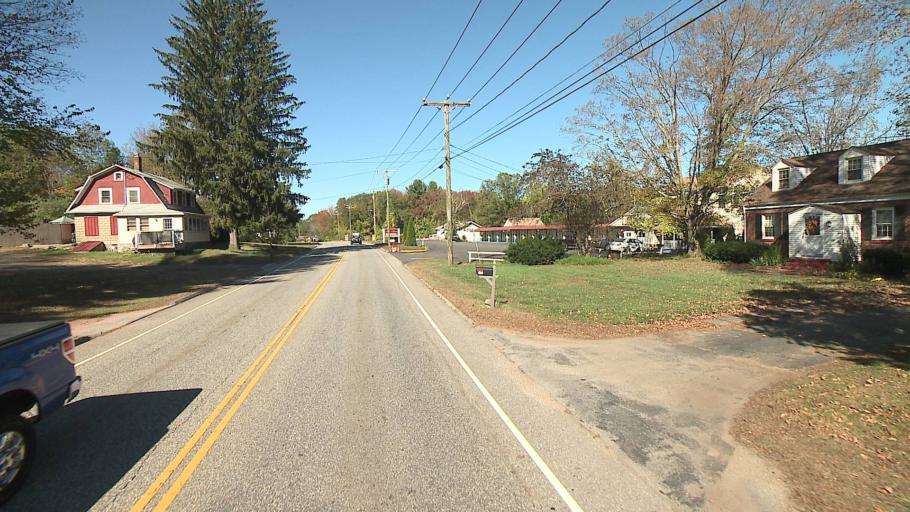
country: US
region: Connecticut
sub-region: Tolland County
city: Mansfield City
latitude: 41.7186
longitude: -72.2689
